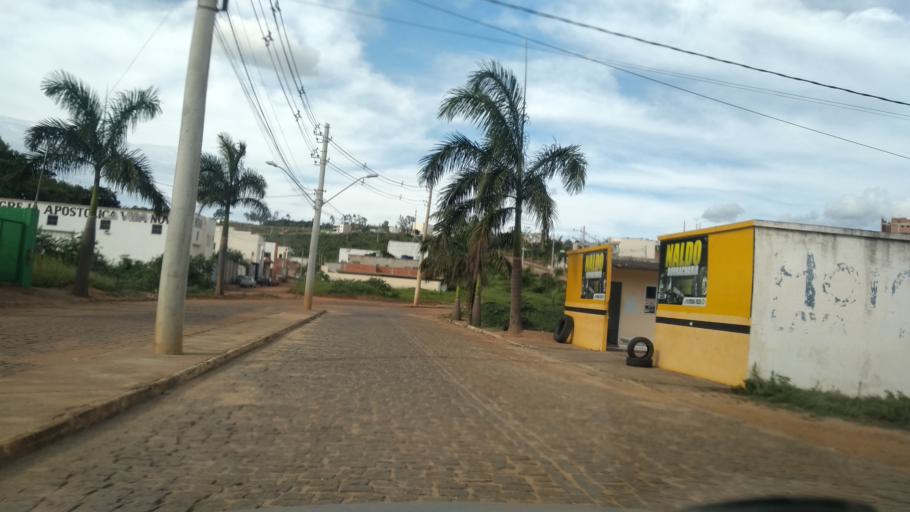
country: BR
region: Bahia
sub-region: Caetite
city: Caetite
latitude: -14.0626
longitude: -42.4969
